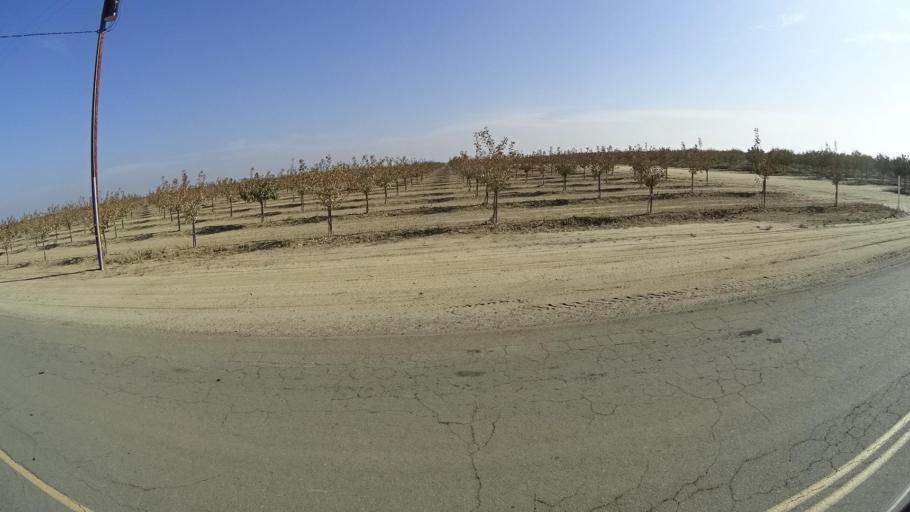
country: US
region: California
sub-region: Kern County
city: McFarland
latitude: 35.6133
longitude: -119.1688
